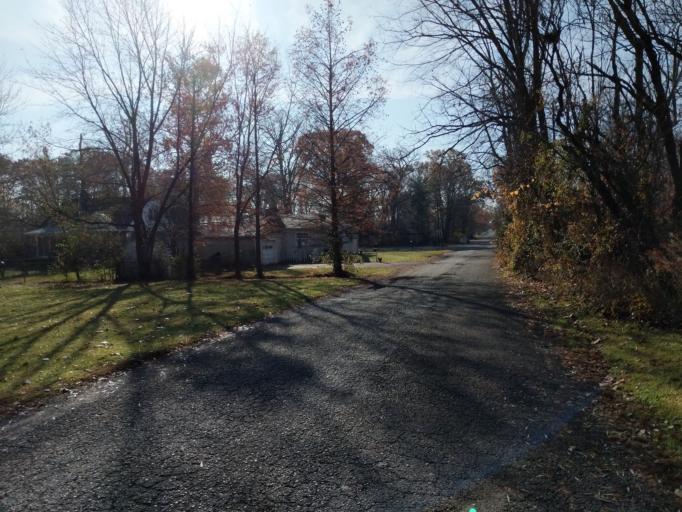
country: US
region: Indiana
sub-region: Marion County
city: Warren Park
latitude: 39.7828
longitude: -86.0133
